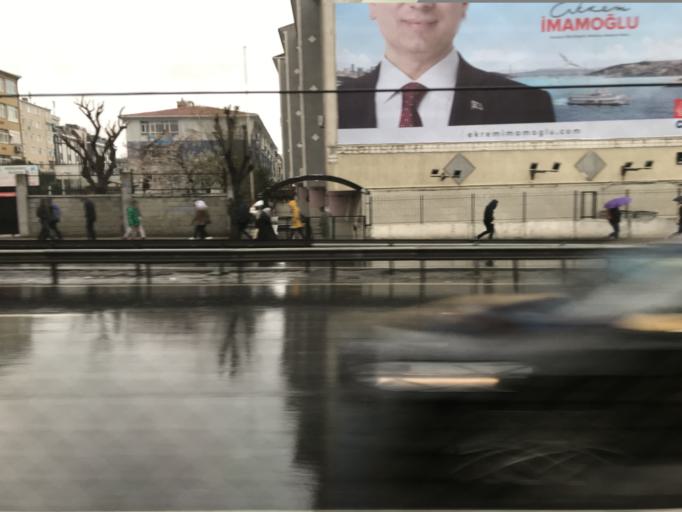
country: TR
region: Istanbul
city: Bahcelievler
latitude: 40.9942
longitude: 28.7951
